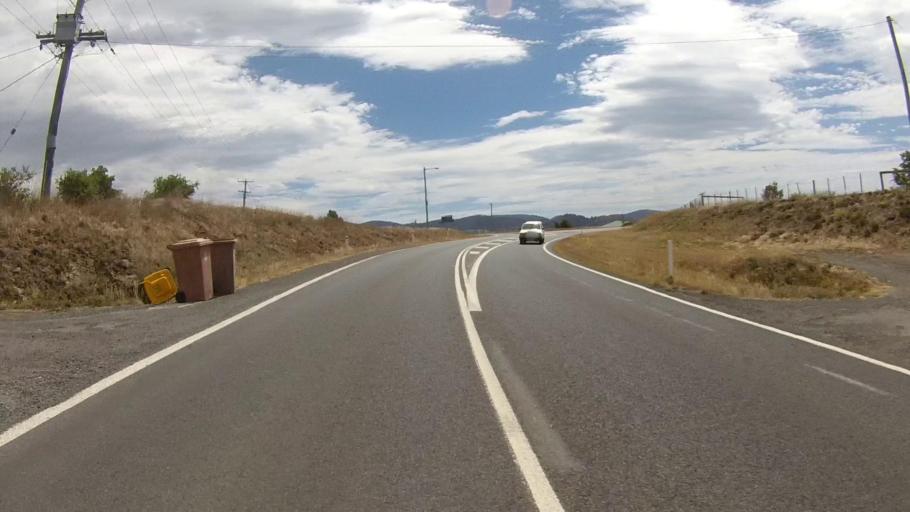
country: AU
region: Tasmania
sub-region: Brighton
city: Bridgewater
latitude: -42.6974
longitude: 147.2695
